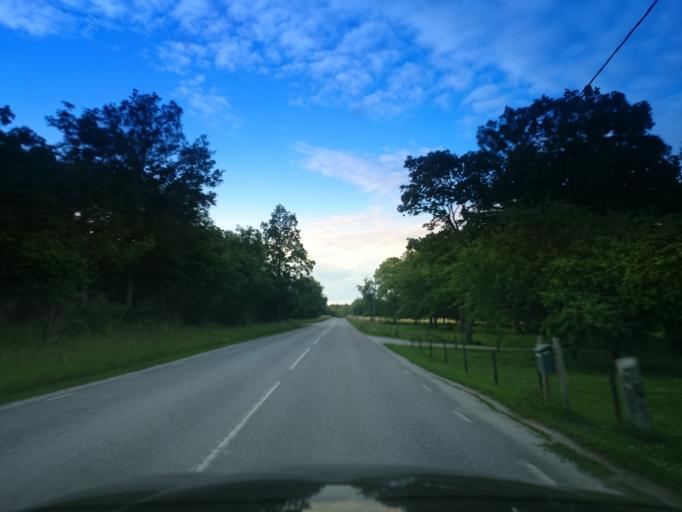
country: SE
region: Gotland
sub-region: Gotland
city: Hemse
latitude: 57.3103
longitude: 18.3805
